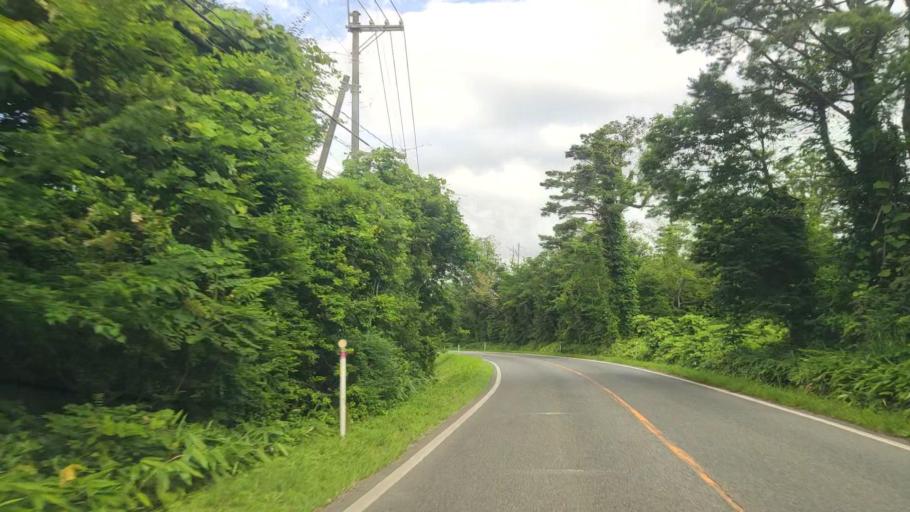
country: JP
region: Tottori
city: Yonago
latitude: 35.4132
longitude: 133.4685
